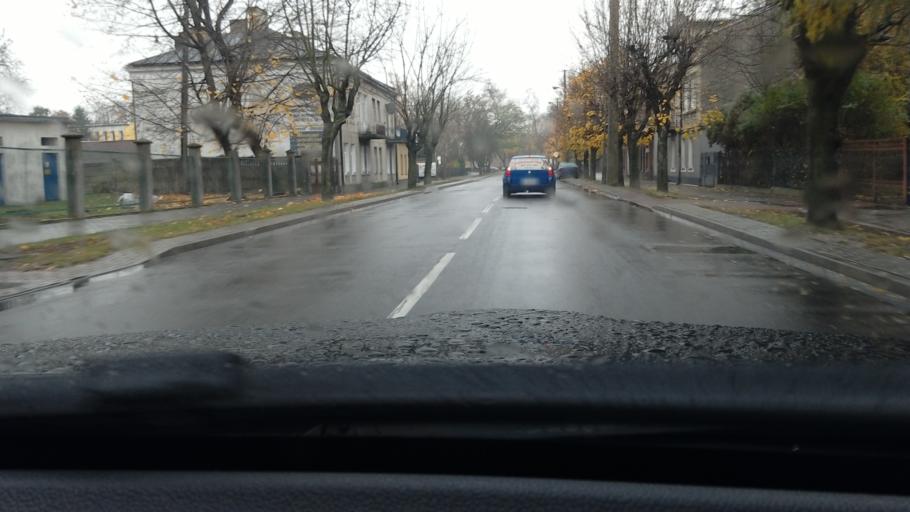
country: PL
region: Lodz Voivodeship
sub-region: Skierniewice
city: Skierniewice
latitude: 51.9506
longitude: 20.1432
